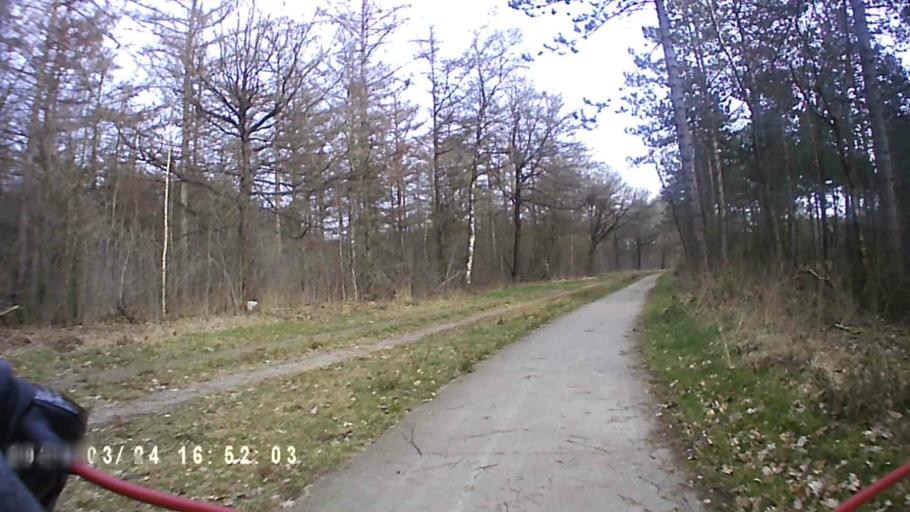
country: NL
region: Groningen
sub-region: Gemeente Leek
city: Leek
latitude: 53.0496
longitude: 6.3035
